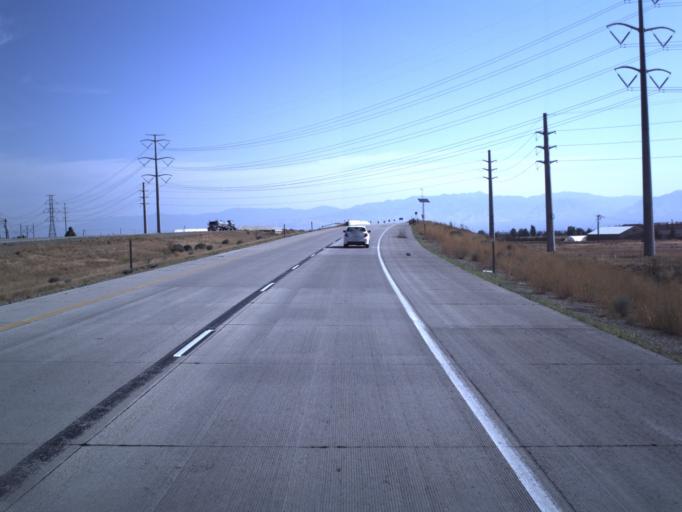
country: US
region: Utah
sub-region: Salt Lake County
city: Oquirrh
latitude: 40.5805
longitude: -112.0318
